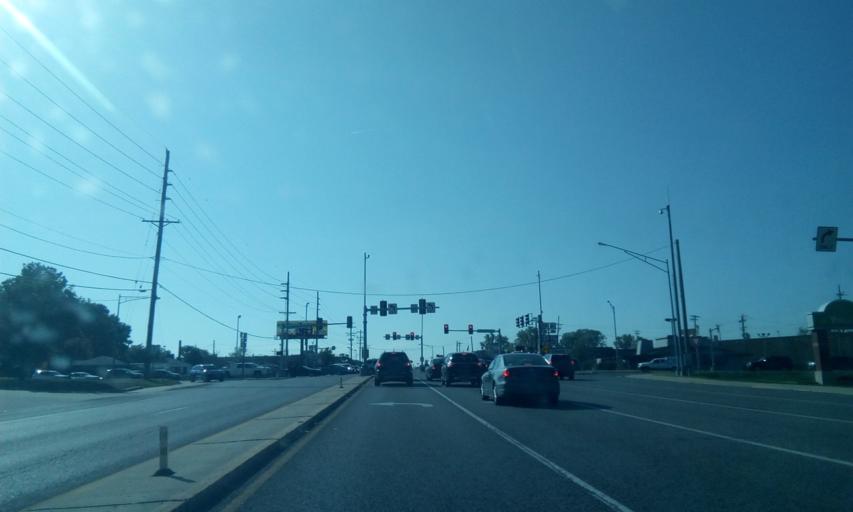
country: US
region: Missouri
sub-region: Saint Louis County
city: Concord
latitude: 38.5236
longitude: -90.3536
